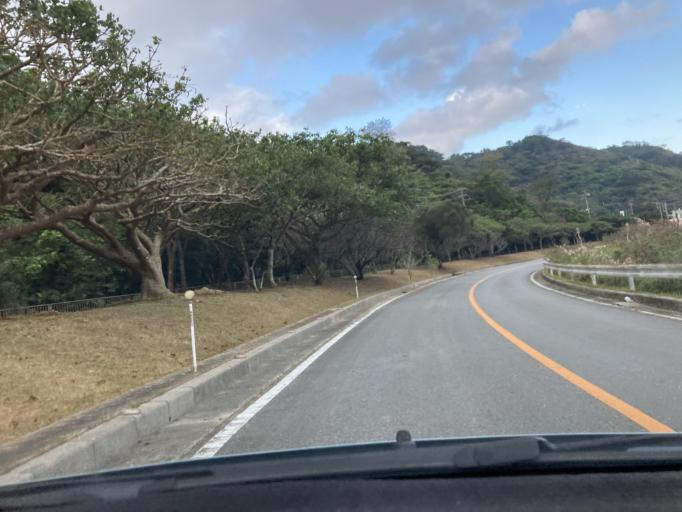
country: JP
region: Okinawa
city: Nago
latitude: 26.8354
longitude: 128.2866
